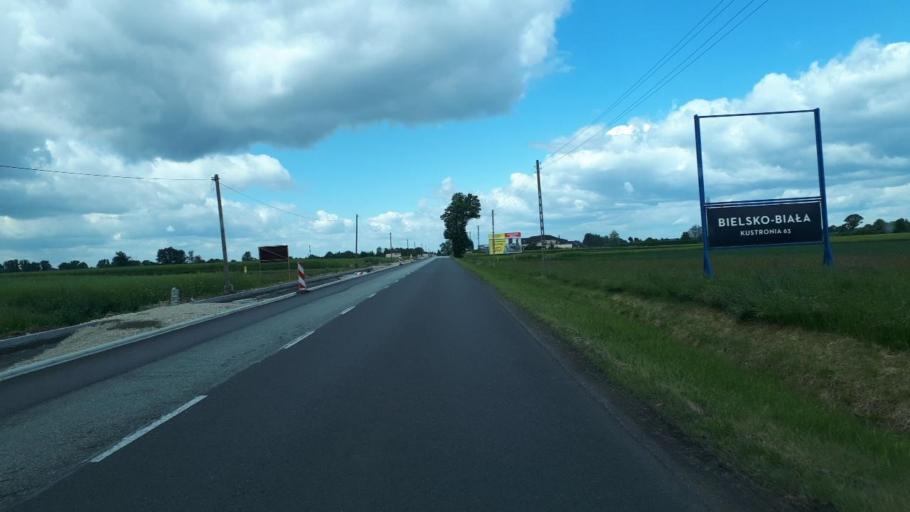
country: PL
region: Silesian Voivodeship
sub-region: Powiat pszczynski
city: Jankowice
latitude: 49.9709
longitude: 19.0070
